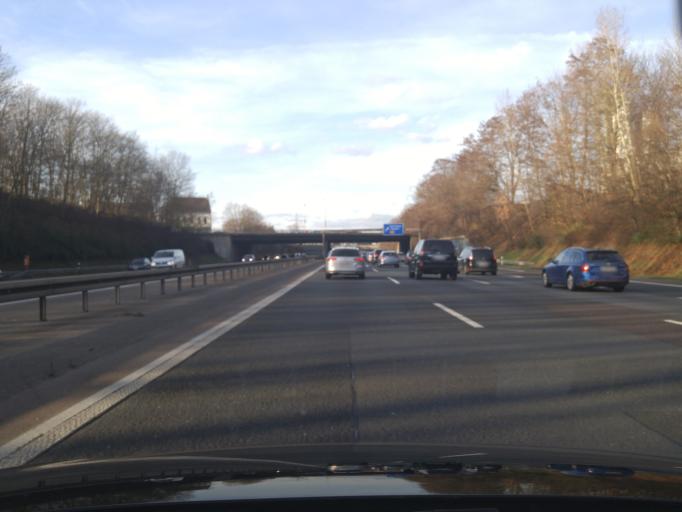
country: DE
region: North Rhine-Westphalia
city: Opladen
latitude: 51.0501
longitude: 6.9997
